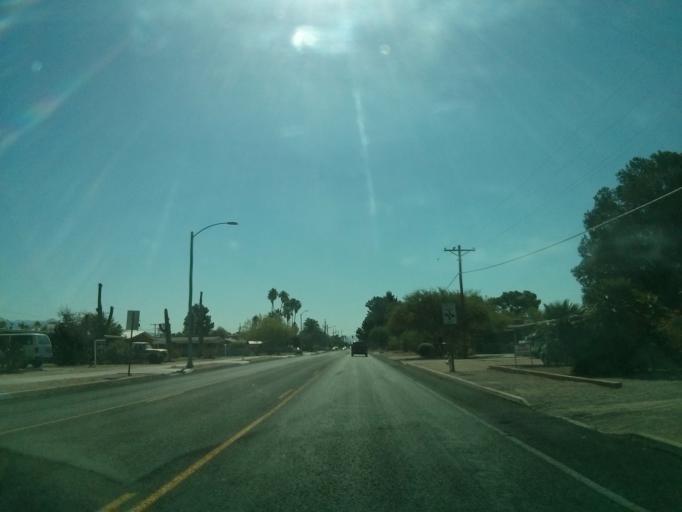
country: US
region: Arizona
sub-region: Pima County
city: Tucson
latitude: 32.2576
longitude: -110.9389
